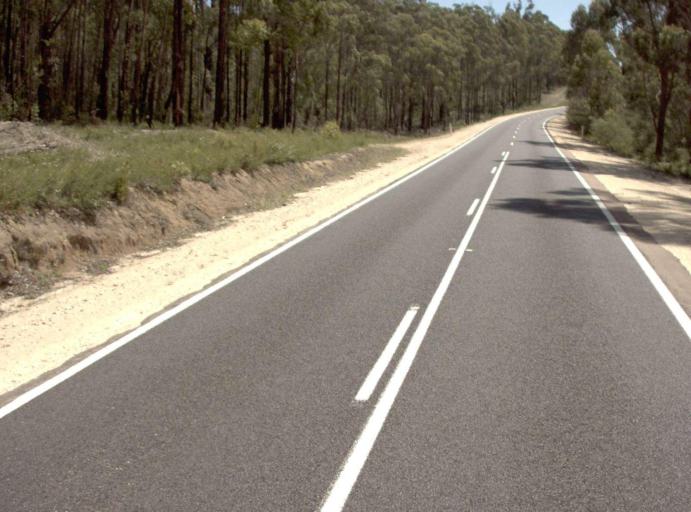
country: AU
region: New South Wales
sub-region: Bombala
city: Bombala
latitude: -37.5666
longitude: 149.1971
